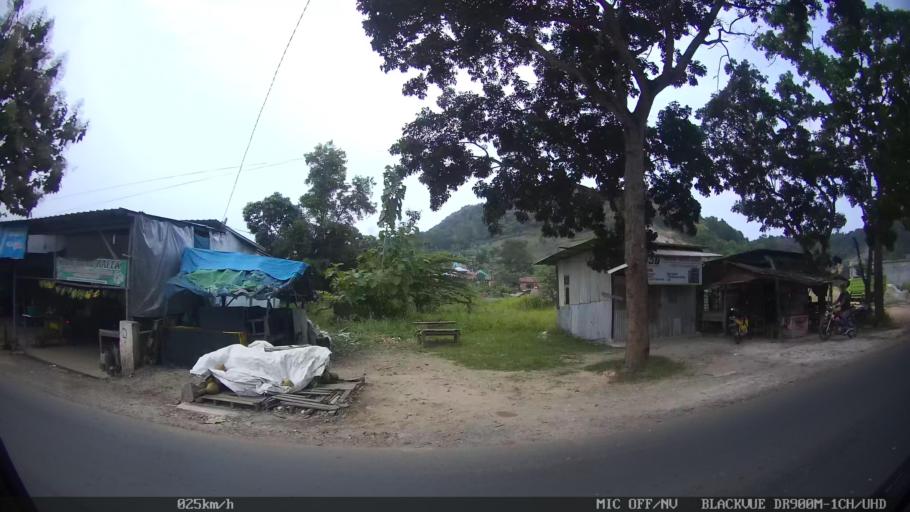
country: ID
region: Lampung
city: Panjang
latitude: -5.4134
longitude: 105.3215
